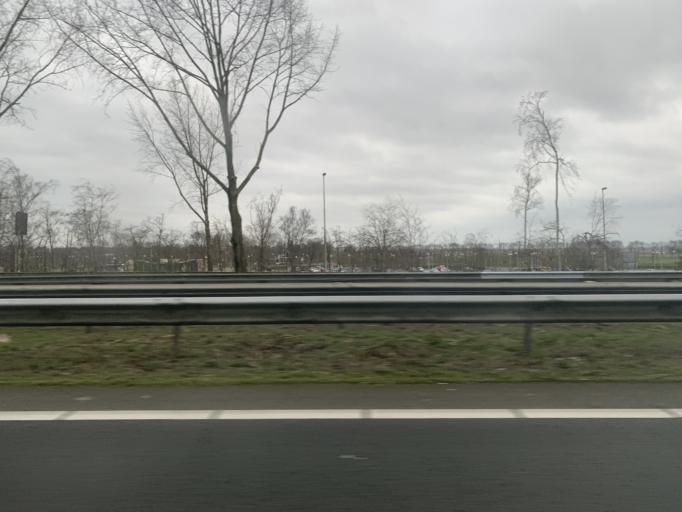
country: NL
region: Groningen
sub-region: Gemeente Groningen
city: Groningen
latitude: 53.1991
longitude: 6.5142
